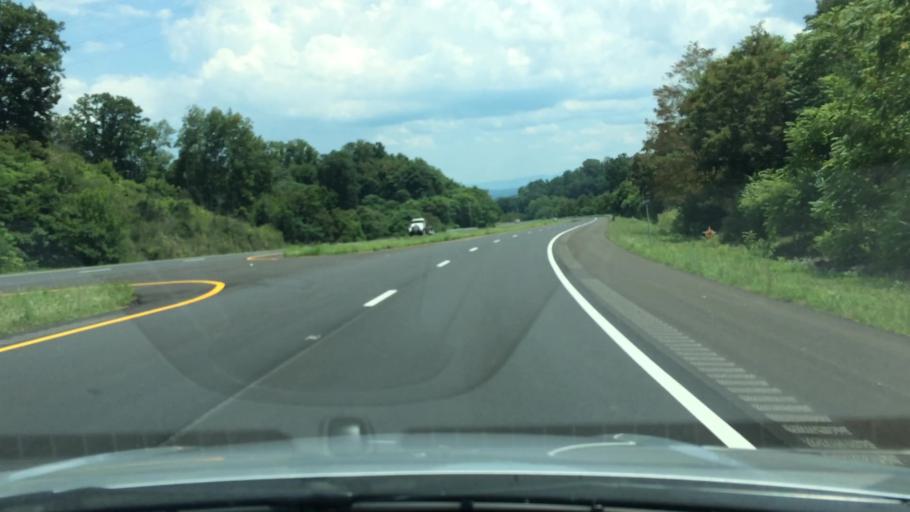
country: US
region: Tennessee
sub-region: Hamblen County
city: Morristown
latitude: 36.1879
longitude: -83.2596
